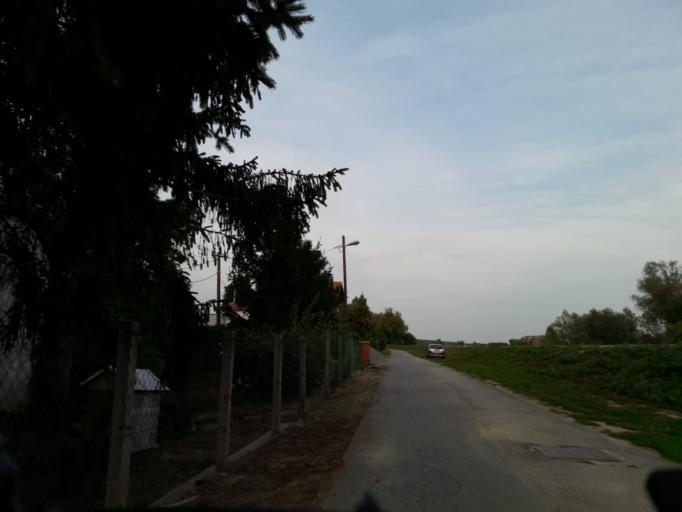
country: HR
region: Osjecko-Baranjska
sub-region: Grad Osijek
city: Osijek
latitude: 45.5618
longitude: 18.7117
